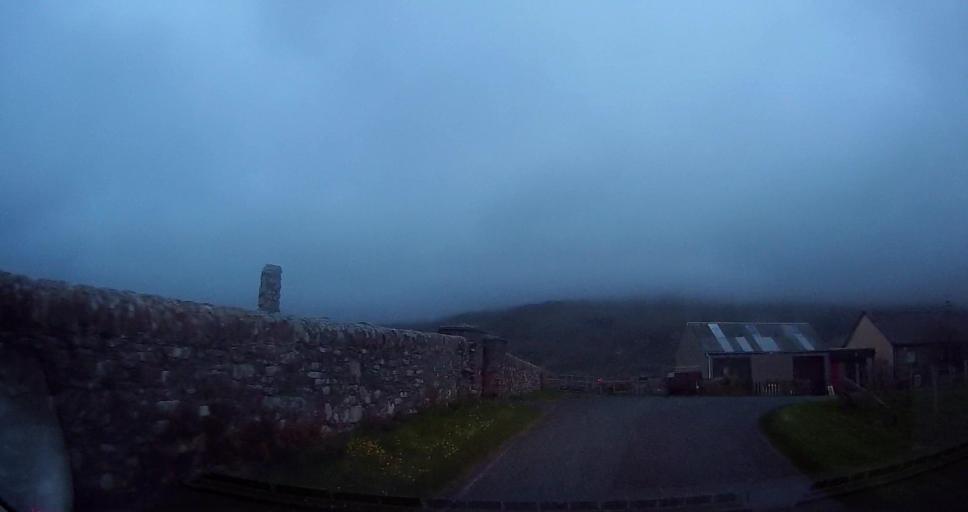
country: GB
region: Scotland
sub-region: Shetland Islands
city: Sandwick
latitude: 60.0341
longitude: -1.2253
